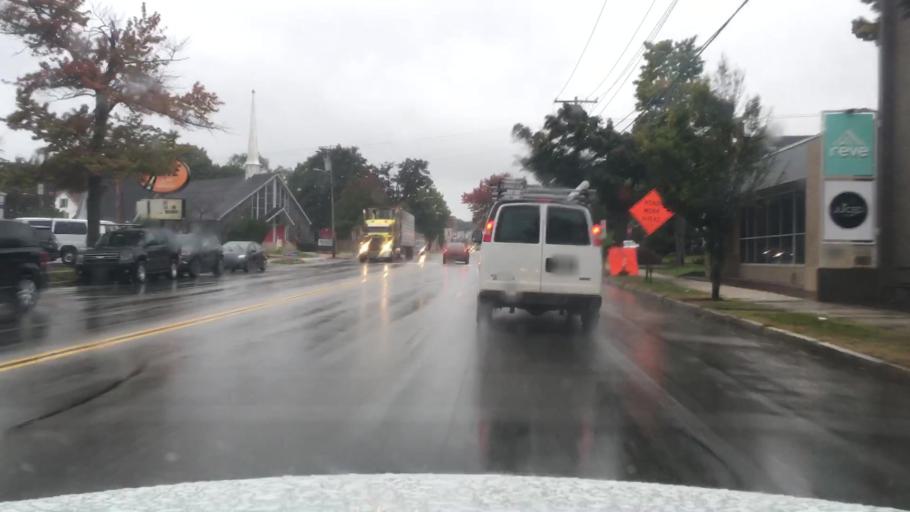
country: US
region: Maine
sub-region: Cumberland County
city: Portland
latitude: 43.6685
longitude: -70.2806
